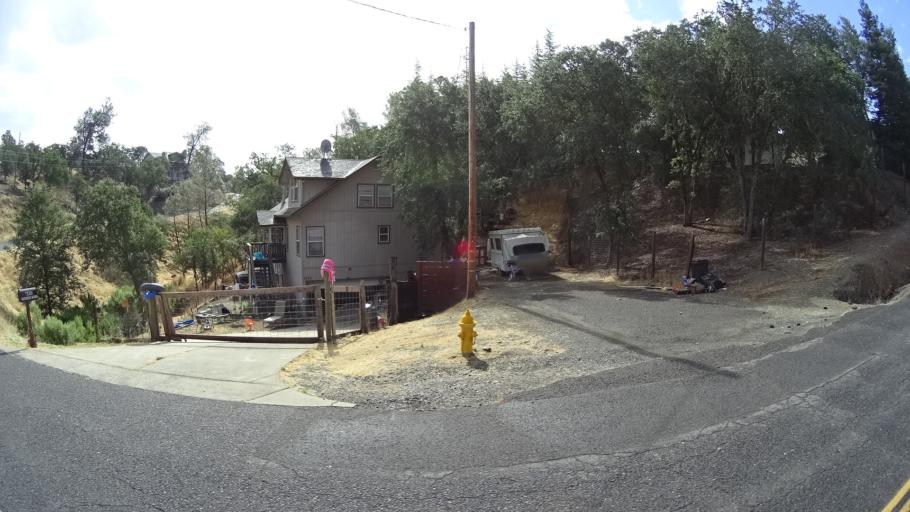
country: US
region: California
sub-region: Calaveras County
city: Copperopolis
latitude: 37.9147
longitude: -120.6071
